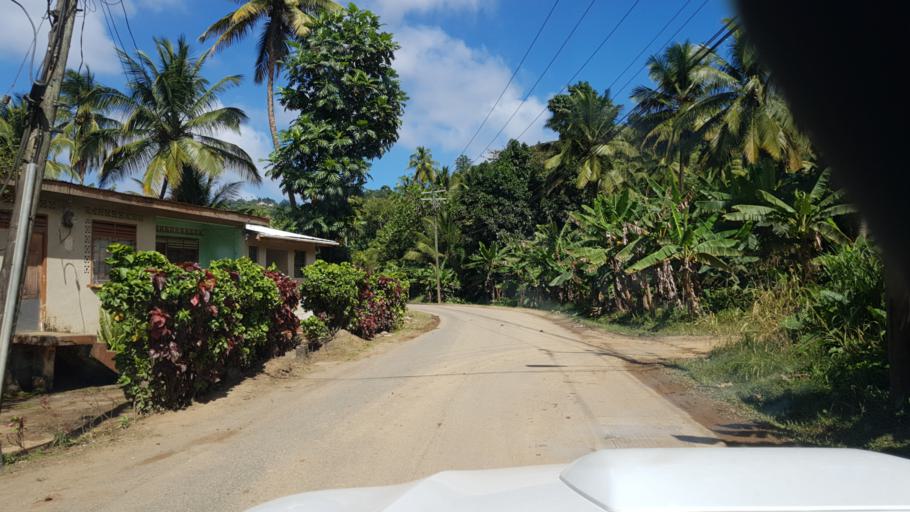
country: LC
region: Castries Quarter
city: Castries
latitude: 13.9778
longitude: -60.9762
